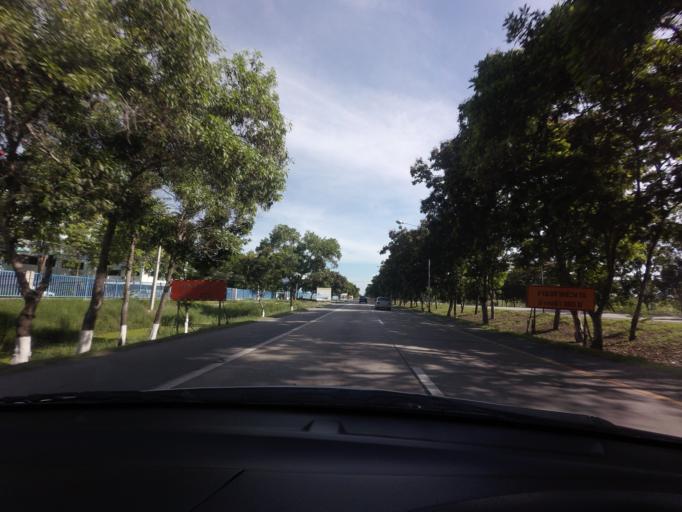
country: TH
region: Suphan Buri
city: Bang Pla Ma
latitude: 14.3558
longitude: 100.1860
